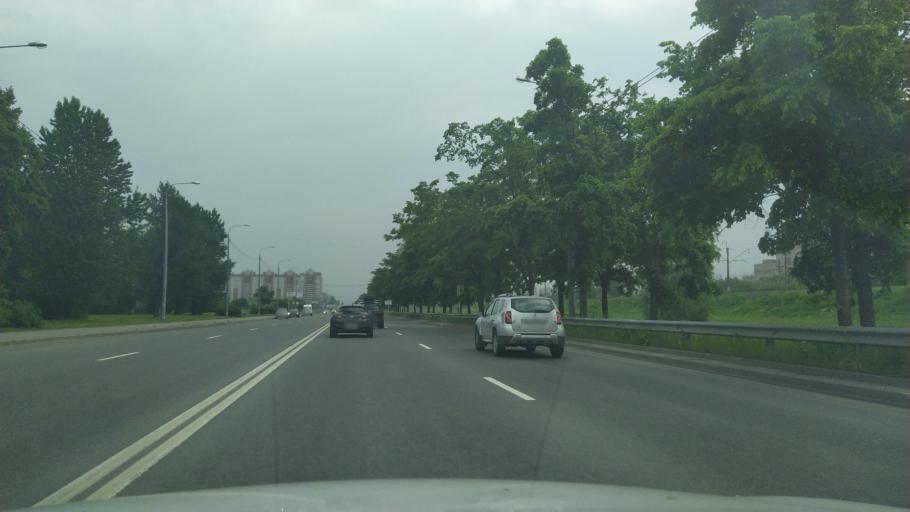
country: RU
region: St.-Petersburg
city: Kupchino
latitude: 59.8689
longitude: 30.3586
